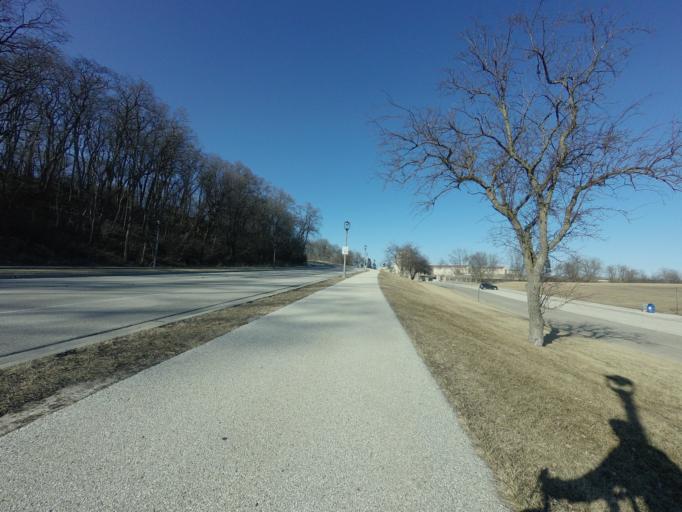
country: US
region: Wisconsin
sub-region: Milwaukee County
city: Shorewood
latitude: 43.0695
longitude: -87.8675
